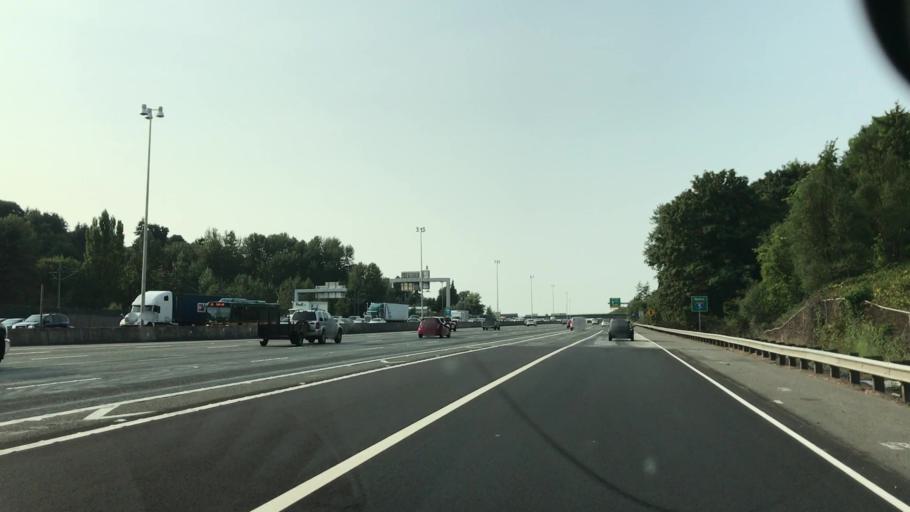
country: US
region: Washington
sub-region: King County
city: Tukwila
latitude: 47.4687
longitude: -122.2675
